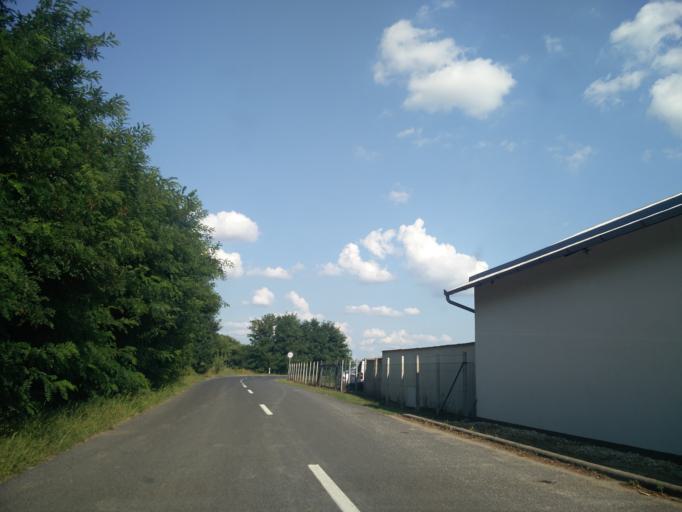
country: HU
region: Zala
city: Zalaegerszeg
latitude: 46.8796
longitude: 16.8269
